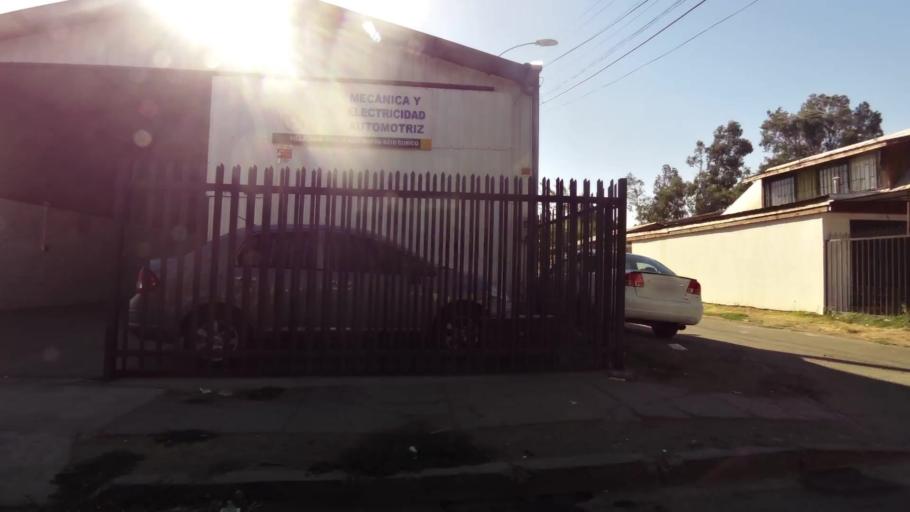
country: CL
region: Maule
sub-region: Provincia de Curico
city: Curico
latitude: -34.9878
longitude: -71.2548
